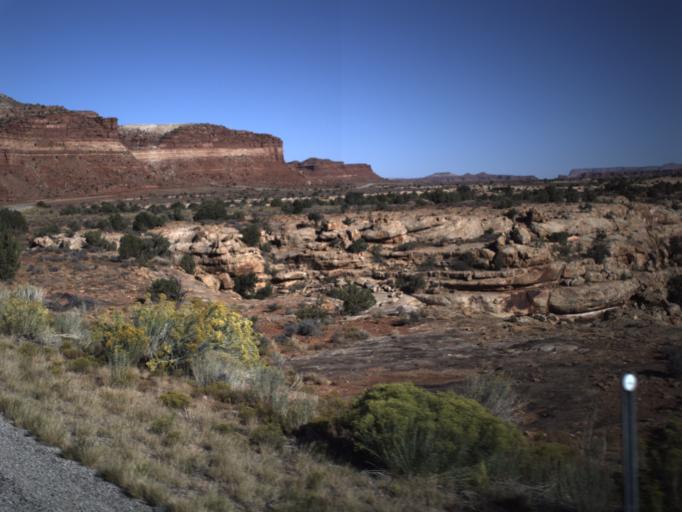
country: US
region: Utah
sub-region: San Juan County
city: Blanding
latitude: 37.7366
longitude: -110.2717
